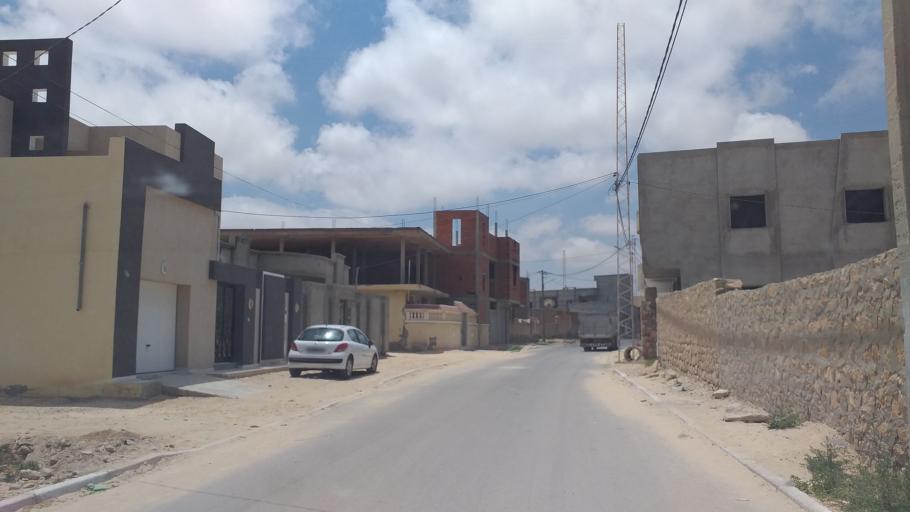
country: TN
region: Qabis
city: Gabes
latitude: 33.9361
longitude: 10.0624
